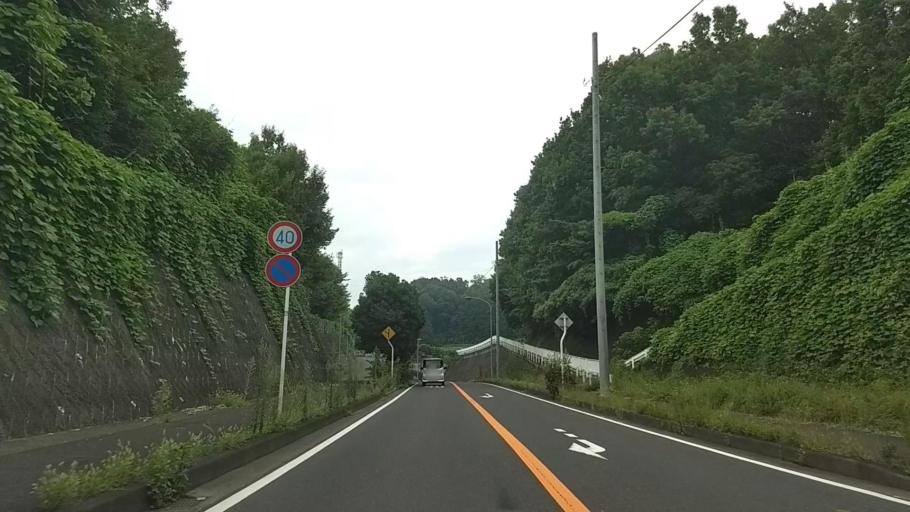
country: JP
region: Kanagawa
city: Hadano
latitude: 35.3386
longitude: 139.2284
